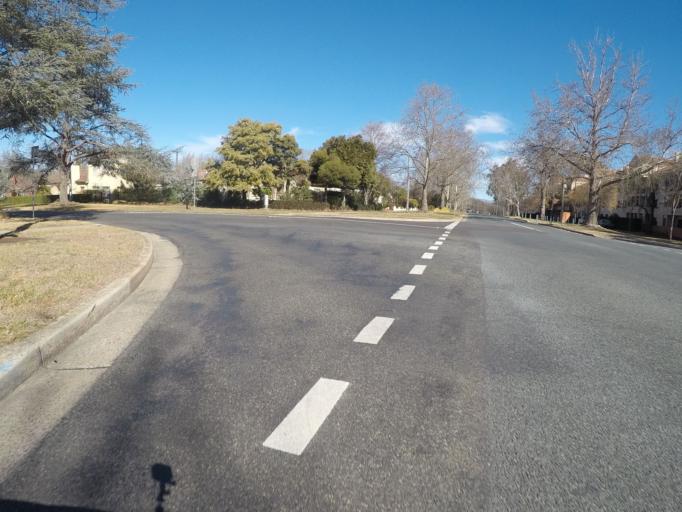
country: AU
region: Australian Capital Territory
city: Canberra
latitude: -35.2813
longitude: 149.1391
